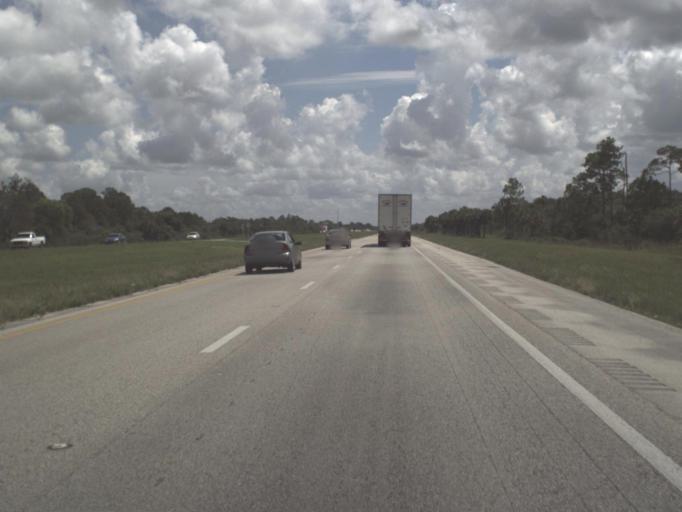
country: US
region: Florida
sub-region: Collier County
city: Orangetree
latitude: 26.1528
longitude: -81.5400
